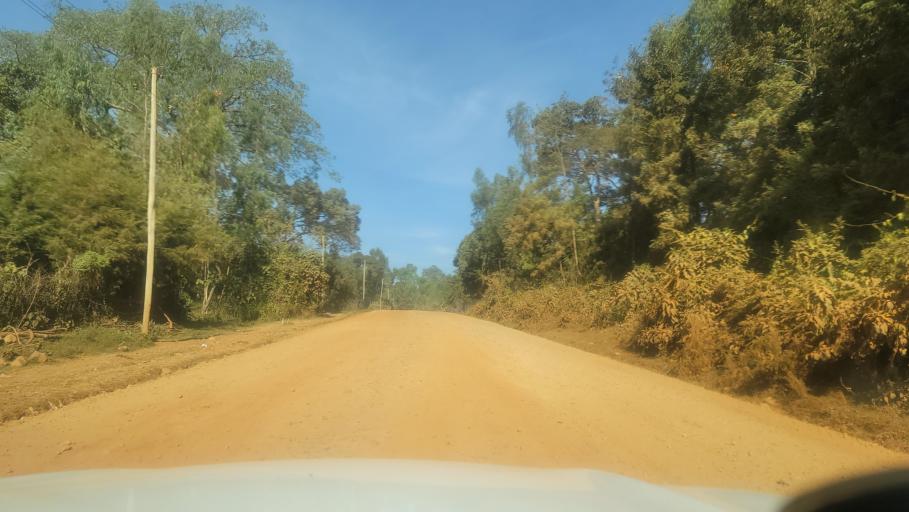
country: ET
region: Oromiya
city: Agaro
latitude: 7.8389
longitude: 36.5519
